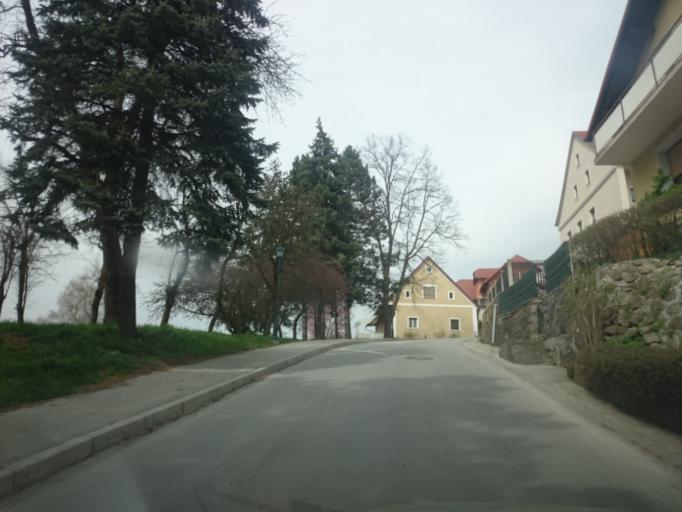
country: SI
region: Sentjur pri Celju
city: Sentjur
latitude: 46.2212
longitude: 15.3961
